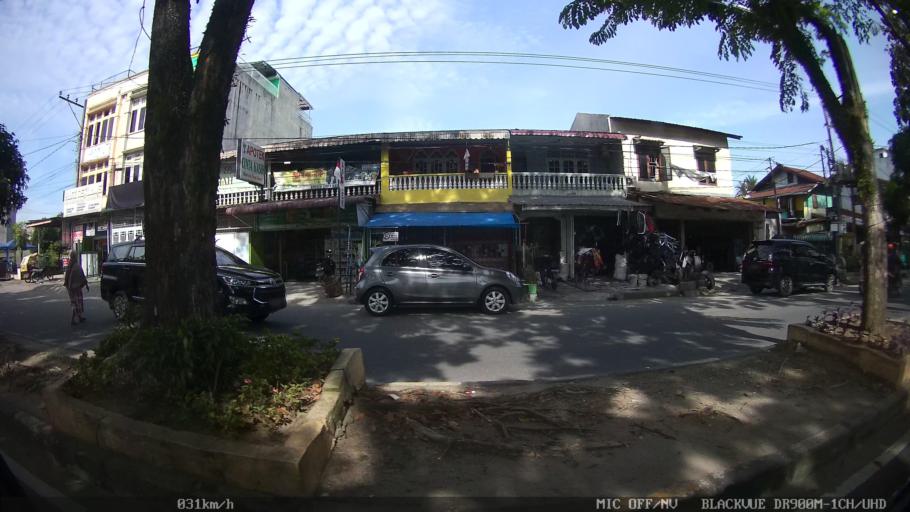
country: ID
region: North Sumatra
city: Medan
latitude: 3.5819
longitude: 98.6433
